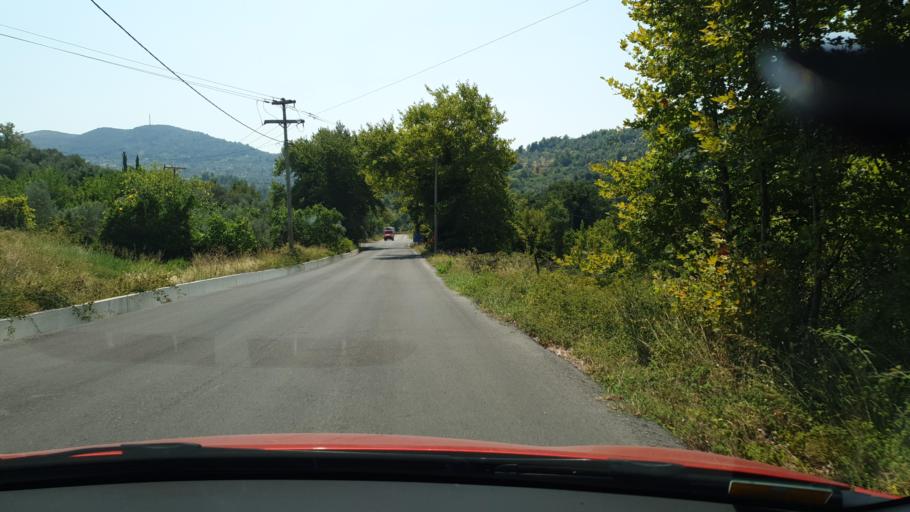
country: GR
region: Central Greece
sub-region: Nomos Evvoias
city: Kymi
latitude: 38.6074
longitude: 24.0735
